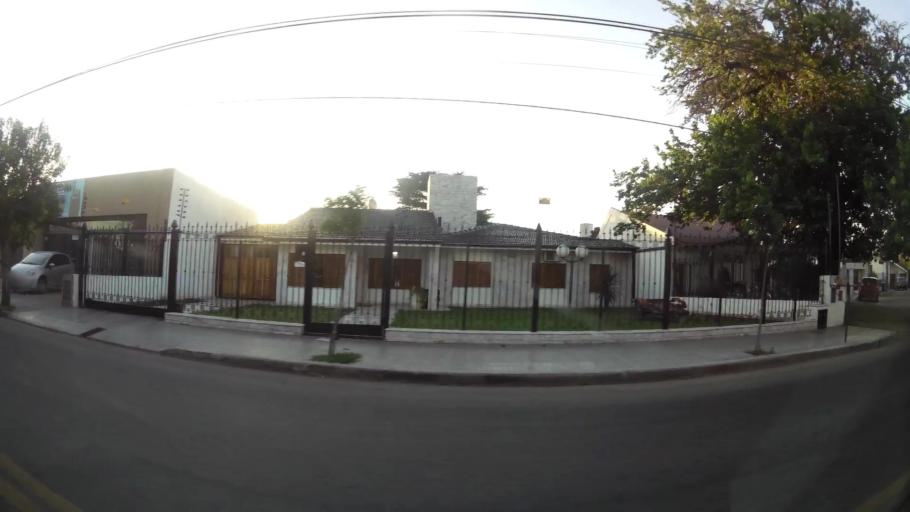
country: AR
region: Cordoba
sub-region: Departamento de Capital
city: Cordoba
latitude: -31.3771
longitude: -64.2230
